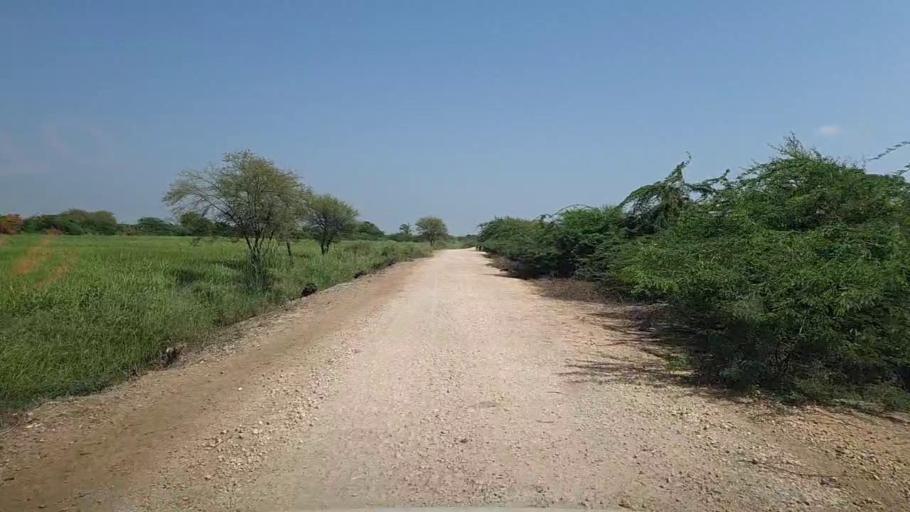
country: PK
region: Sindh
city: Kario
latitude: 24.8358
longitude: 68.7110
